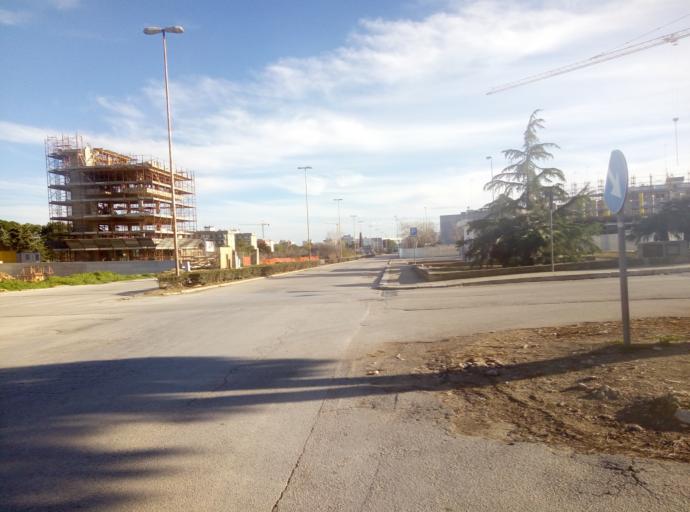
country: IT
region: Apulia
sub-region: Provincia di Bari
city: Ruvo di Puglia
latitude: 41.1198
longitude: 16.4913
